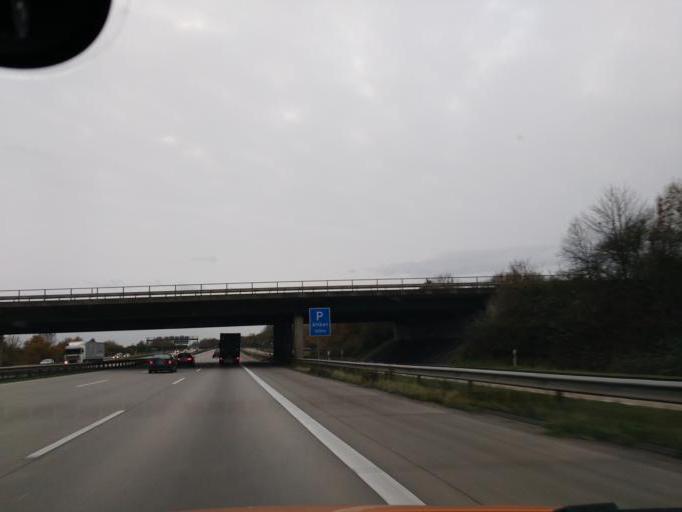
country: DE
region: Bremen
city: Bremen
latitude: 53.0296
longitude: 8.8597
